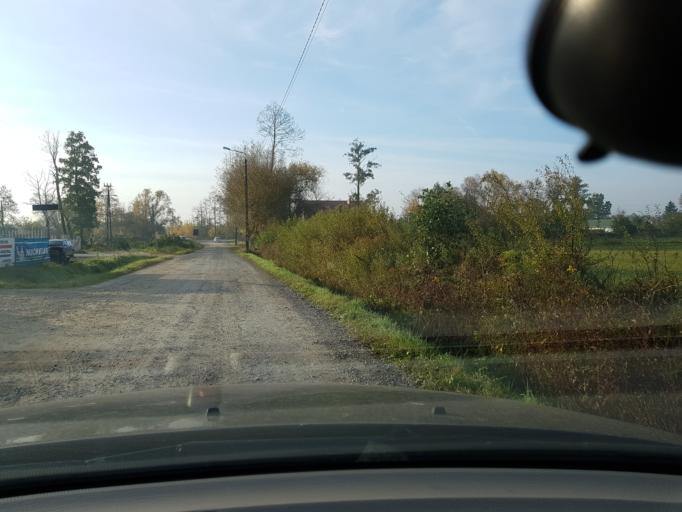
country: PL
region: Masovian Voivodeship
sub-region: Powiat minski
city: Halinow
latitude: 52.1883
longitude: 21.3129
